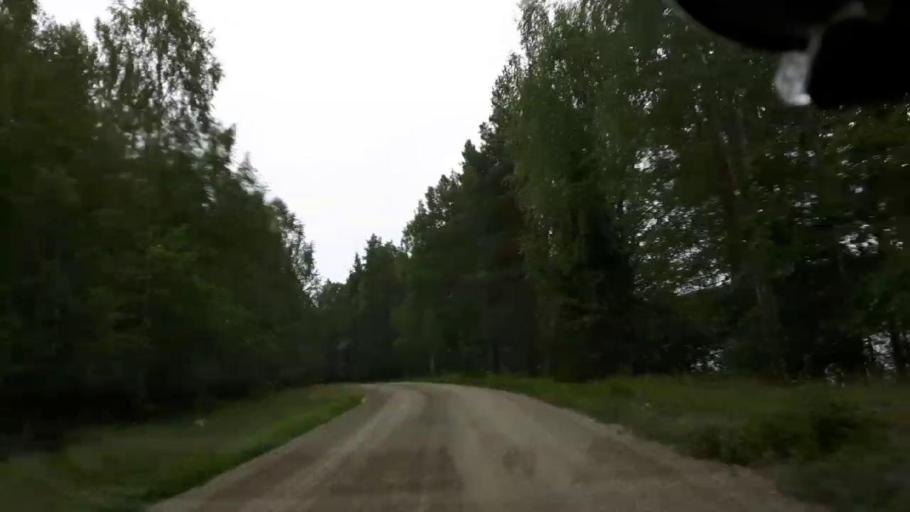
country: SE
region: Jaemtland
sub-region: Braecke Kommun
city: Braecke
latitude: 62.9850
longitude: 15.3907
